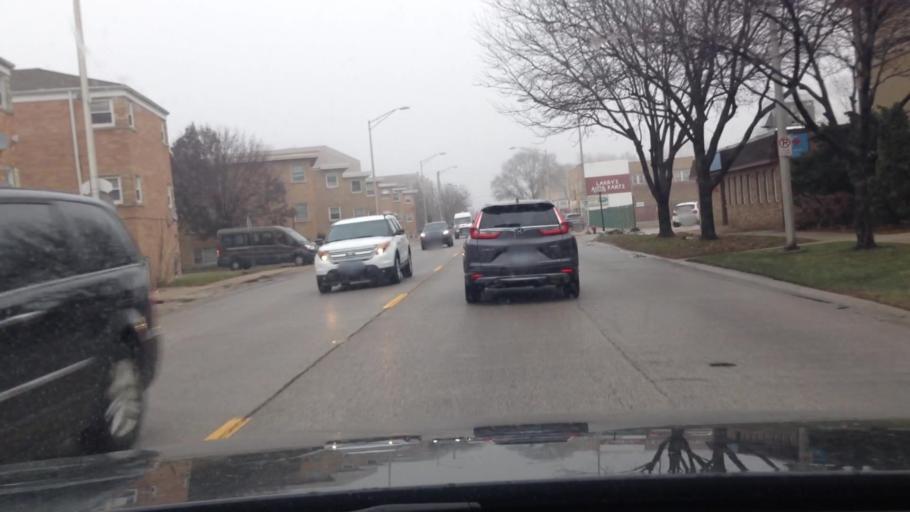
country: US
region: Illinois
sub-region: Cook County
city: River Grove
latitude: 41.9274
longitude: -87.8278
